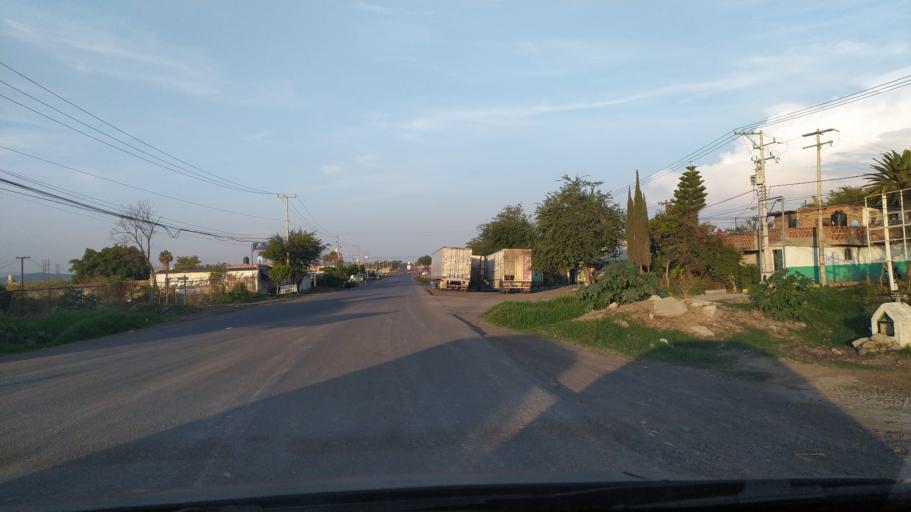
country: MX
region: Michoacan
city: Vistahermosa de Negrete
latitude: 20.2661
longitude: -102.4734
